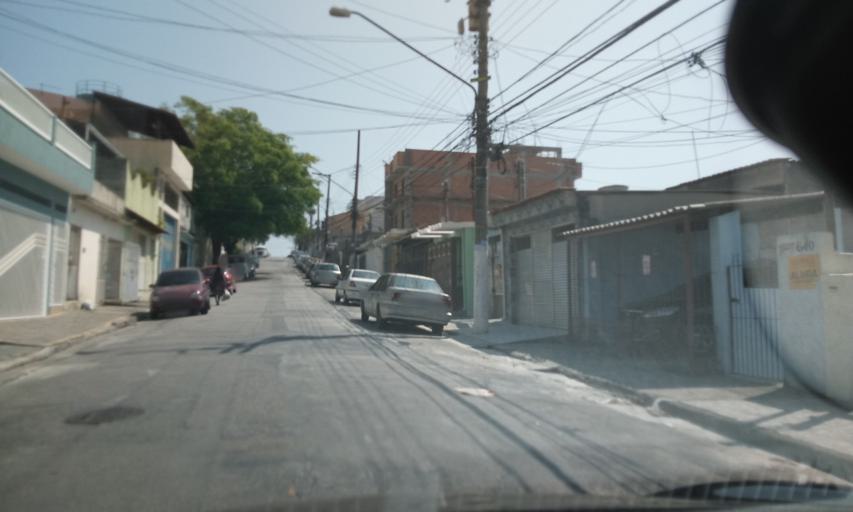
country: BR
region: Sao Paulo
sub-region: Sao Bernardo Do Campo
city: Sao Bernardo do Campo
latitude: -23.6977
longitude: -46.5690
